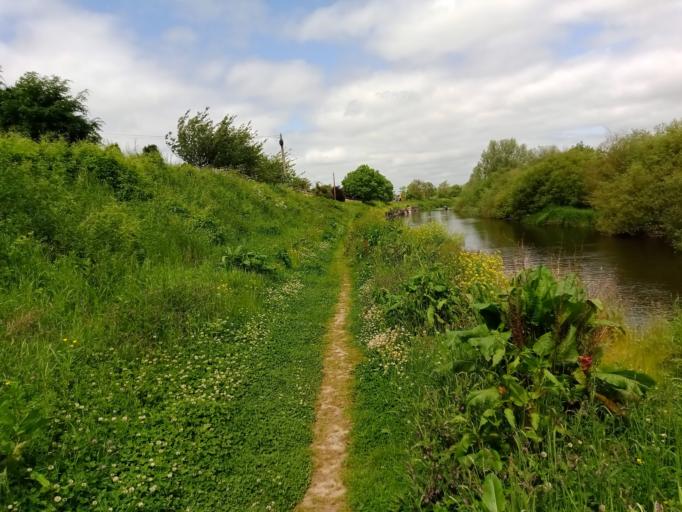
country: IE
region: Leinster
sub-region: County Carlow
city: Carlow
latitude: 52.8053
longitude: -6.9665
